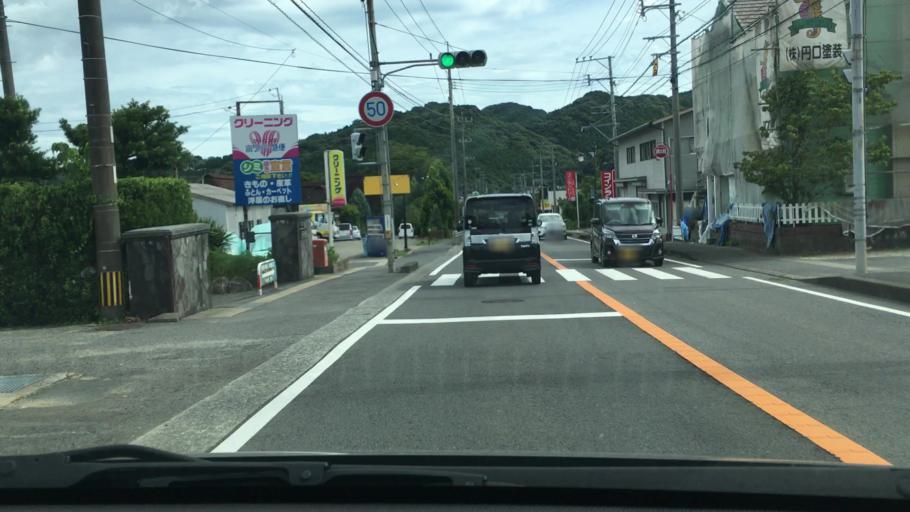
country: JP
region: Nagasaki
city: Togitsu
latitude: 32.8986
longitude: 129.7810
